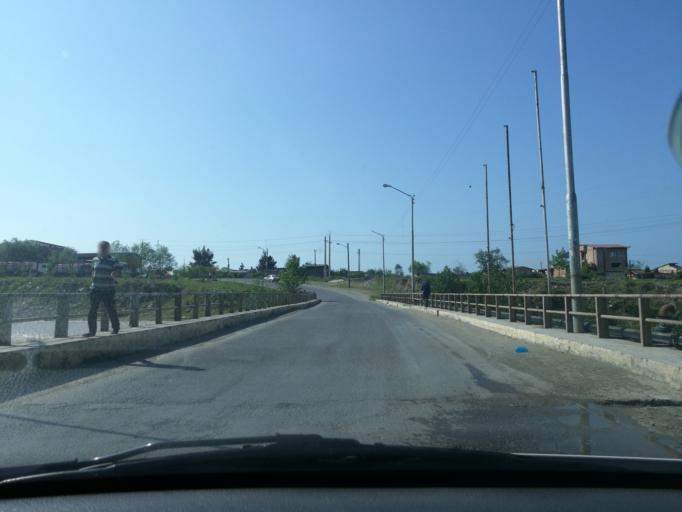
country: IR
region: Mazandaran
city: Chalus
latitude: 36.6590
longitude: 51.4370
